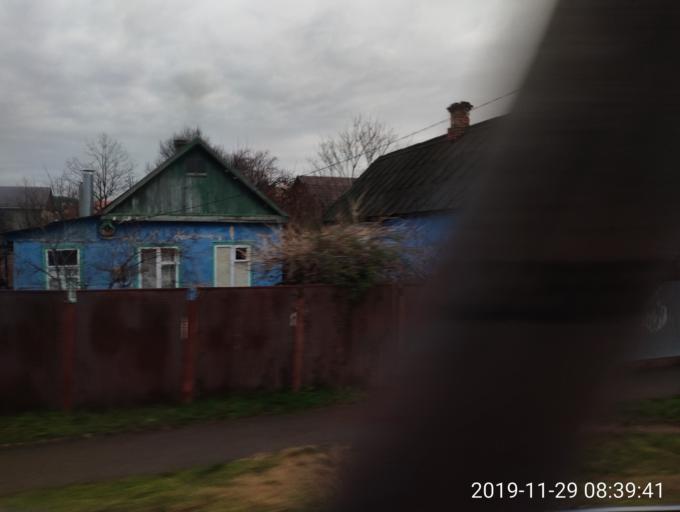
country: RU
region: Krasnodarskiy
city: Krasnodar
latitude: 45.0480
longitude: 38.9970
